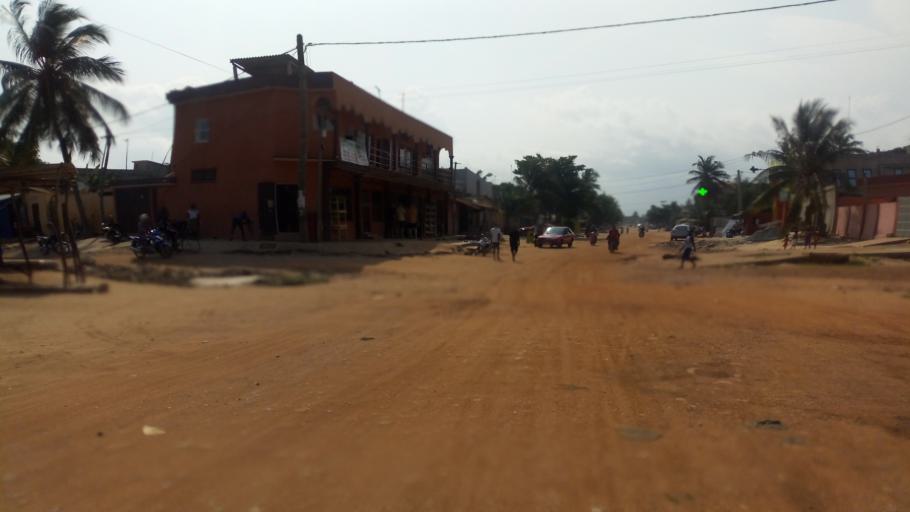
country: TG
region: Maritime
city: Lome
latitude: 6.1919
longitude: 1.1819
